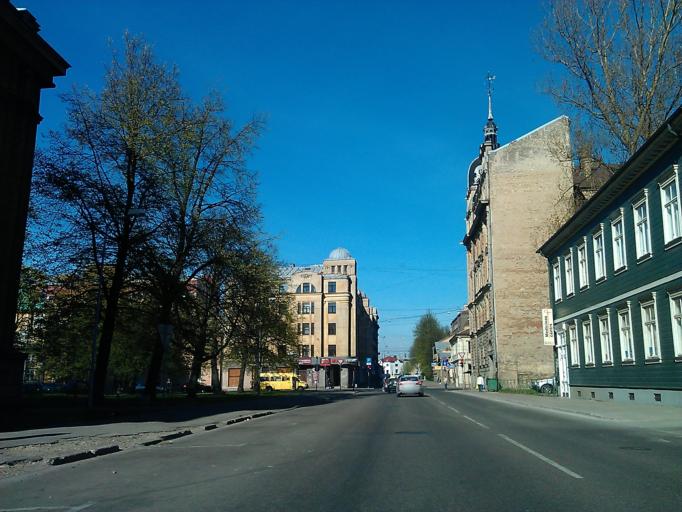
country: LV
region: Riga
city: Riga
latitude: 56.9426
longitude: 24.1226
